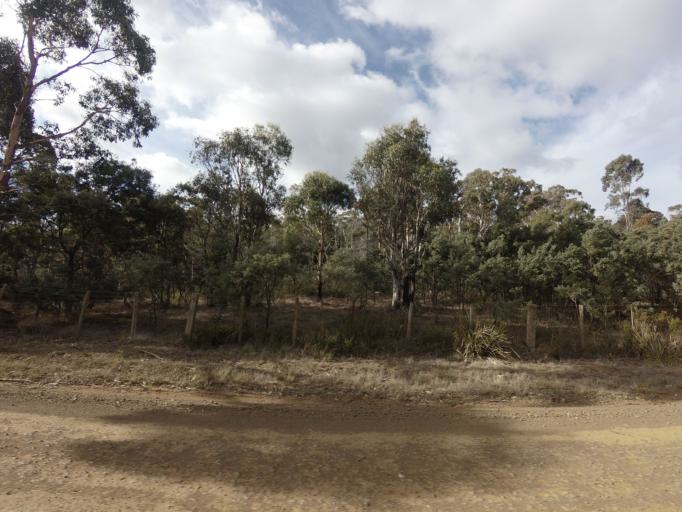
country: AU
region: Tasmania
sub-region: Brighton
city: Bridgewater
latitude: -42.4798
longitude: 147.2948
